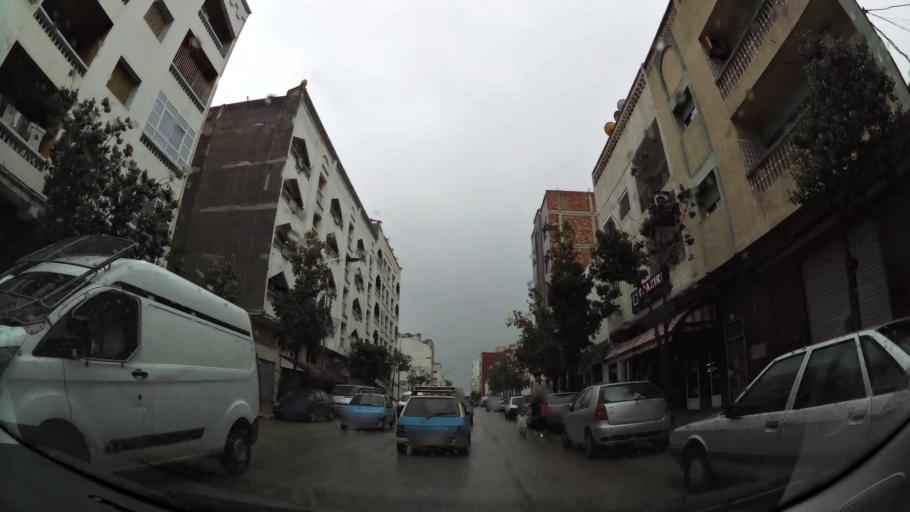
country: MA
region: Taza-Al Hoceima-Taounate
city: Al Hoceima
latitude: 35.2503
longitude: -3.9373
